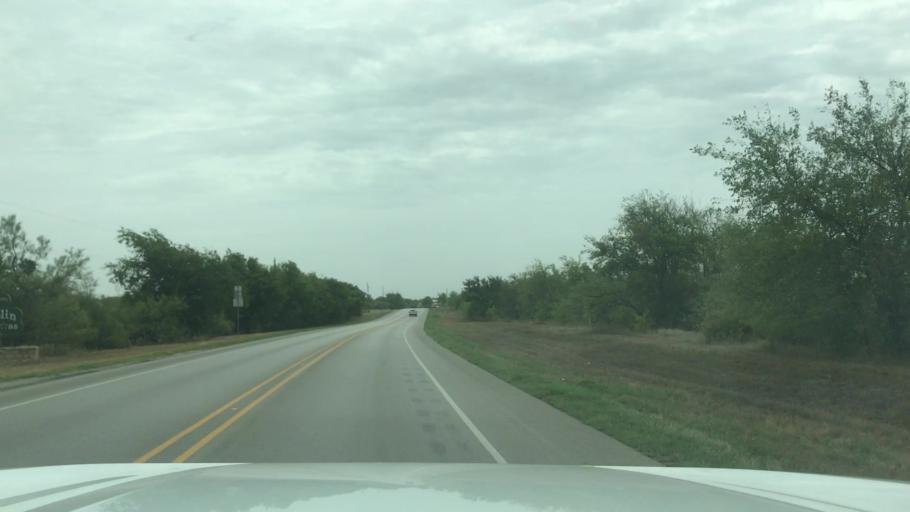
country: US
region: Texas
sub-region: Erath County
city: Dublin
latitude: 32.0916
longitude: -98.3634
